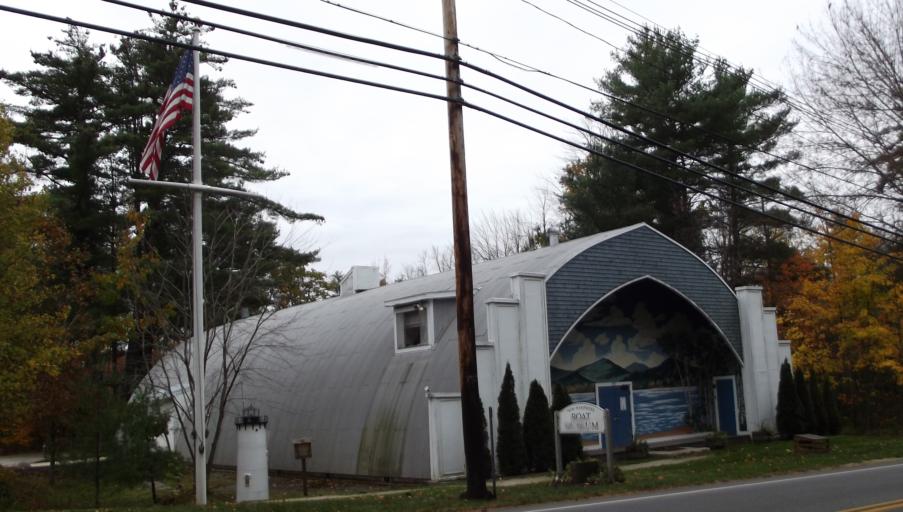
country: US
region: New Hampshire
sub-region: Carroll County
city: Wolfeboro
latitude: 43.6058
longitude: -71.1884
